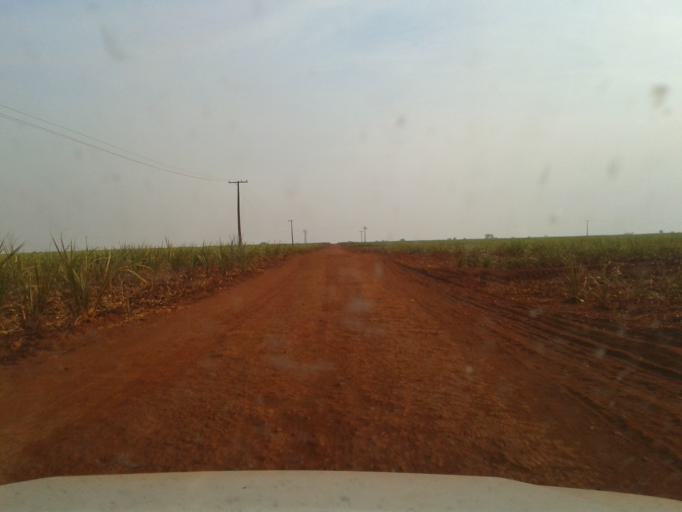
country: BR
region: Minas Gerais
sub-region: Capinopolis
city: Capinopolis
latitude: -18.7354
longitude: -49.6881
